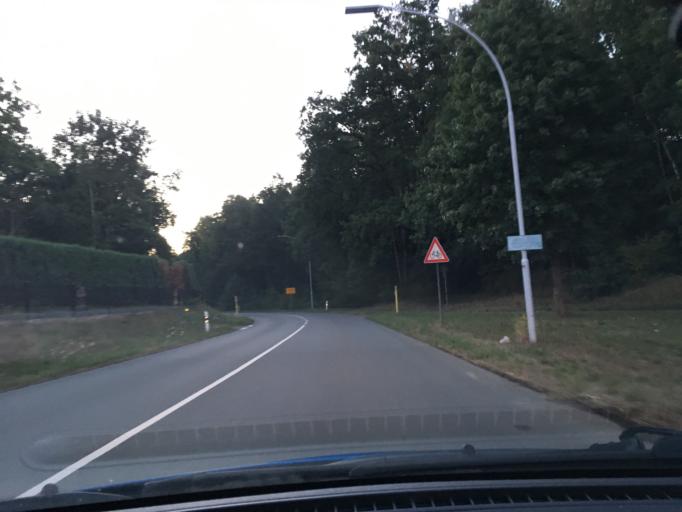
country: DE
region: Lower Saxony
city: Fassberg
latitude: 52.9263
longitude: 10.1397
